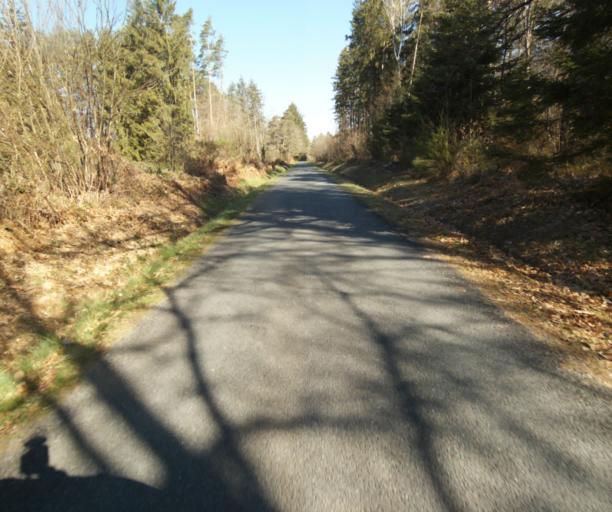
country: FR
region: Limousin
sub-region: Departement de la Correze
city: Correze
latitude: 45.2738
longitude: 1.9244
